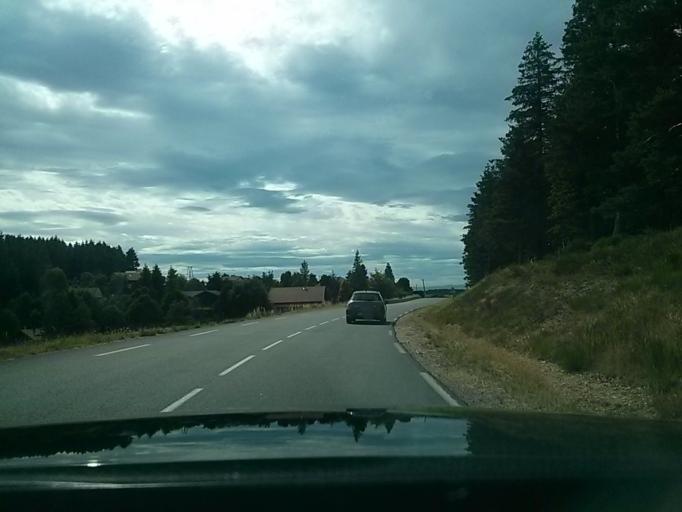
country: FR
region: Rhone-Alpes
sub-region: Departement de la Loire
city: Saint-Genest-Malifaux
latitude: 45.3730
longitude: 4.4989
